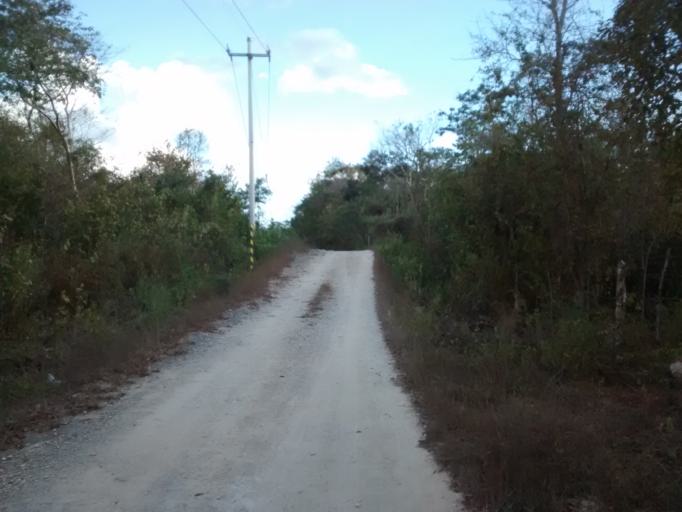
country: MX
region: Yucatan
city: Chichimila
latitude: 20.4491
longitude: -88.2017
